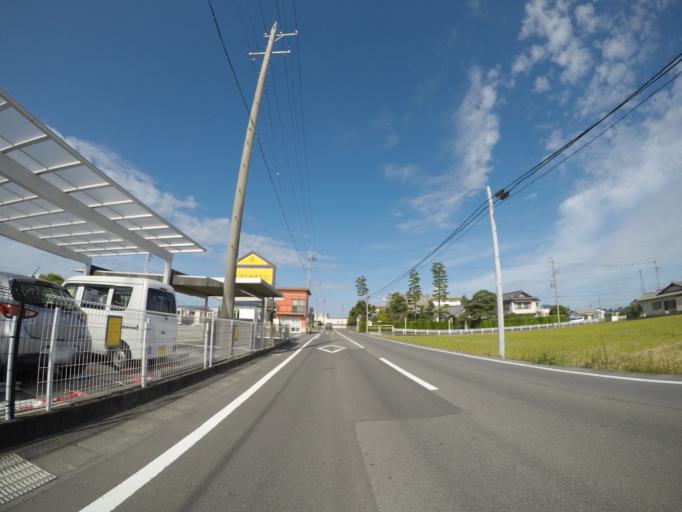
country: JP
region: Shizuoka
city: Fujieda
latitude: 34.8376
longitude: 138.2850
